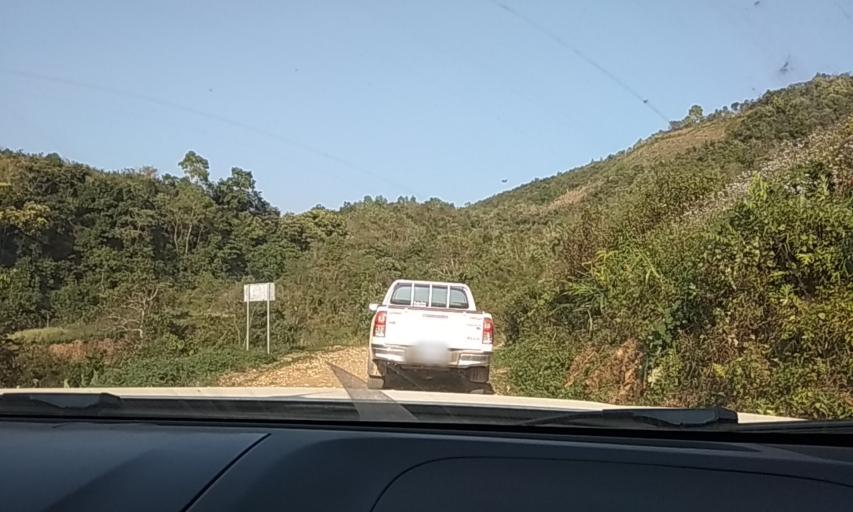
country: LA
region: Phongsali
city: Phongsali
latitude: 21.6745
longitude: 102.1890
